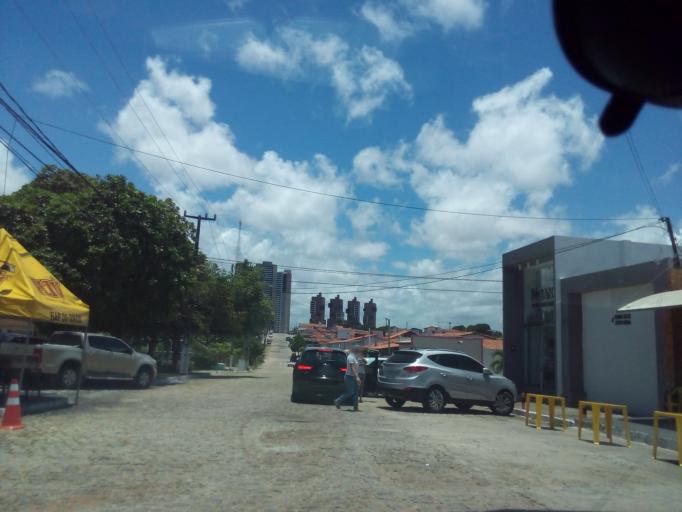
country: BR
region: Rio Grande do Norte
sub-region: Natal
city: Natal
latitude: -5.8437
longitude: -35.2035
